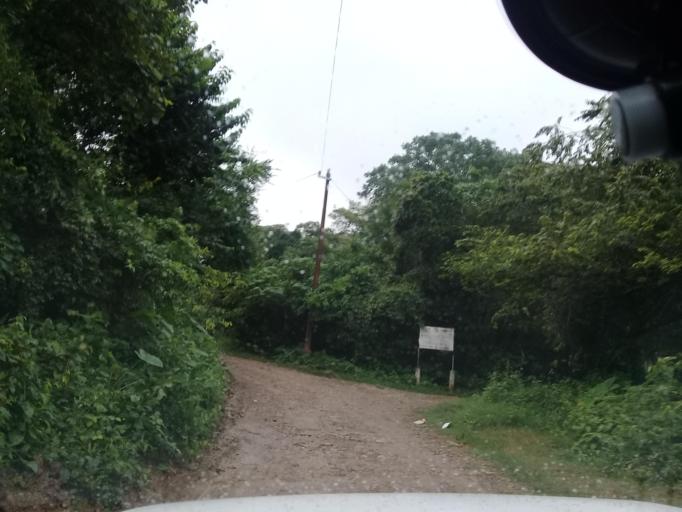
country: MX
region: Veracruz
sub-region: Chalma
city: San Pedro Coyutla
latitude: 21.2417
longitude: -98.4204
